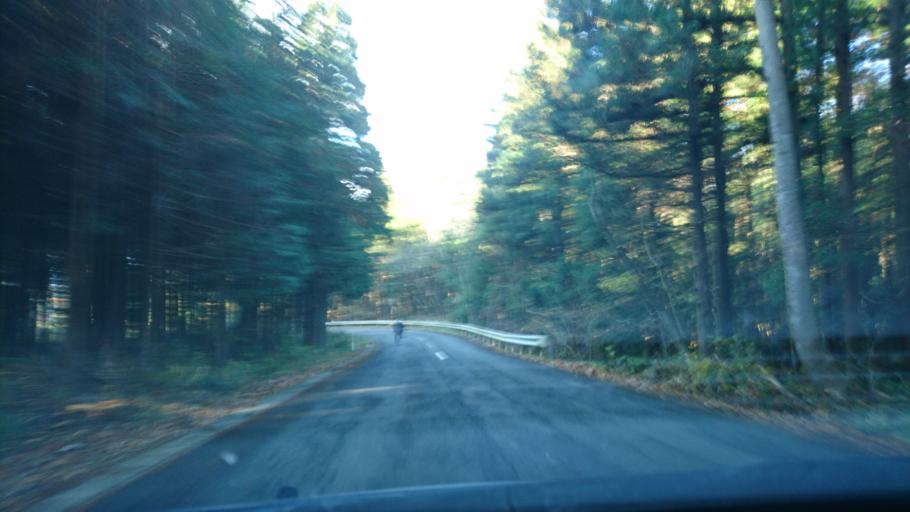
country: JP
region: Iwate
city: Mizusawa
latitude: 39.0328
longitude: 141.1587
